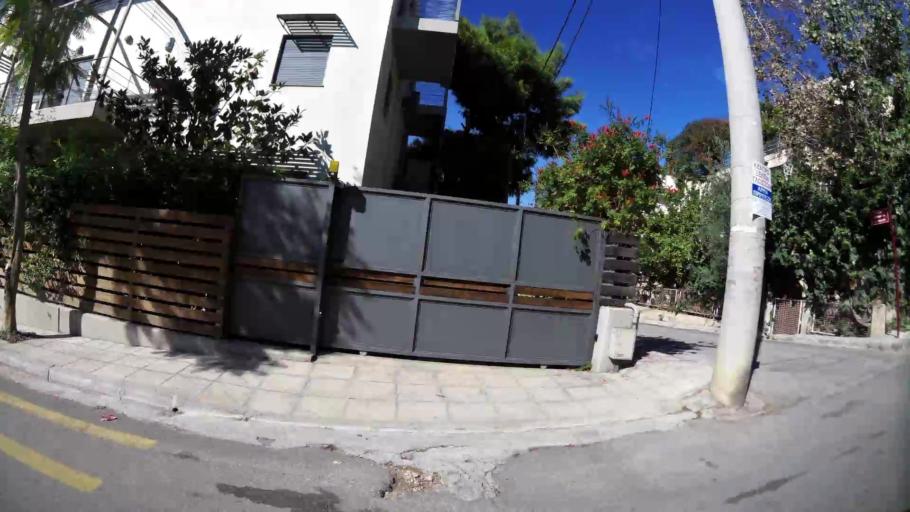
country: GR
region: Attica
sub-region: Nomarchia Athinas
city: Metamorfosi
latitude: 38.0648
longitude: 23.7670
